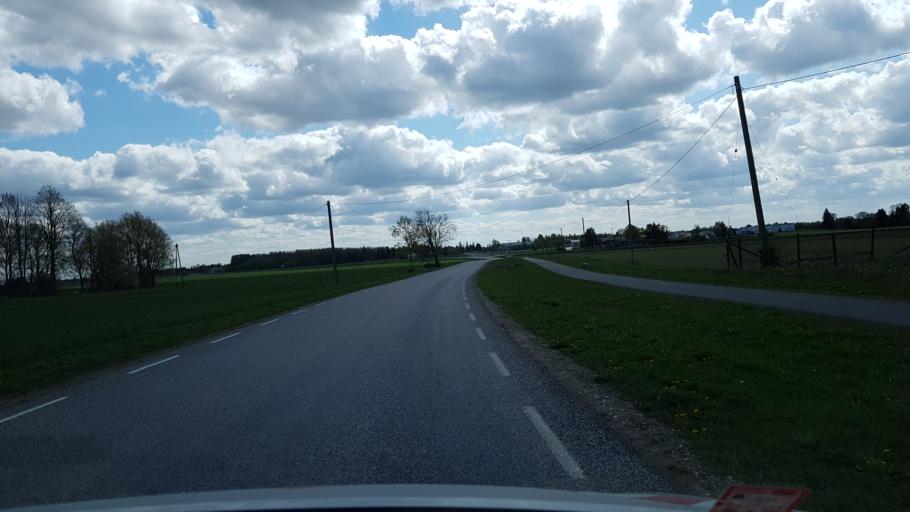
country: EE
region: Jogevamaa
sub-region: Poltsamaa linn
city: Poltsamaa
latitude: 58.6749
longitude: 25.9598
